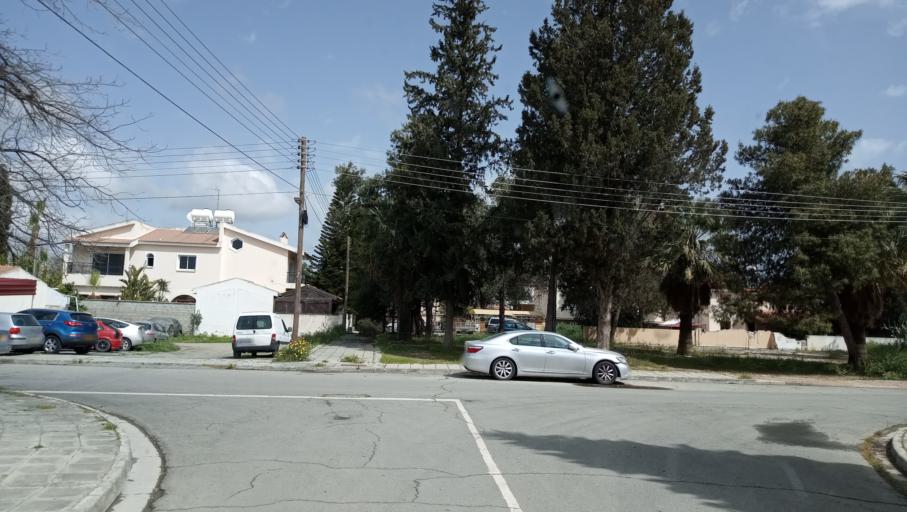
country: CY
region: Lefkosia
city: Dali
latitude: 35.0217
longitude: 33.4253
